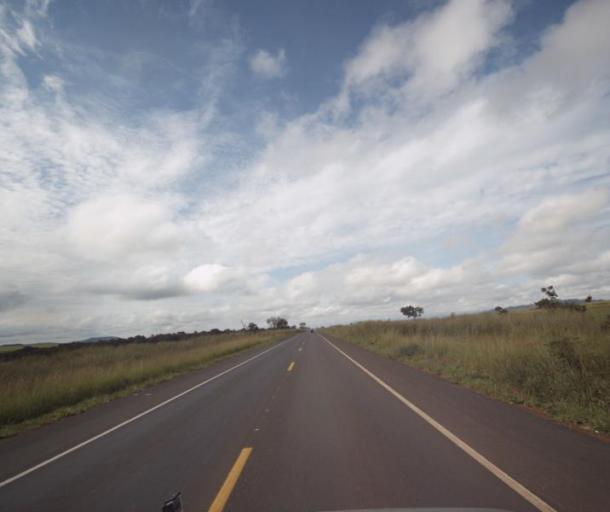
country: BR
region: Goias
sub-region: Padre Bernardo
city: Padre Bernardo
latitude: -15.4487
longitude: -48.6168
